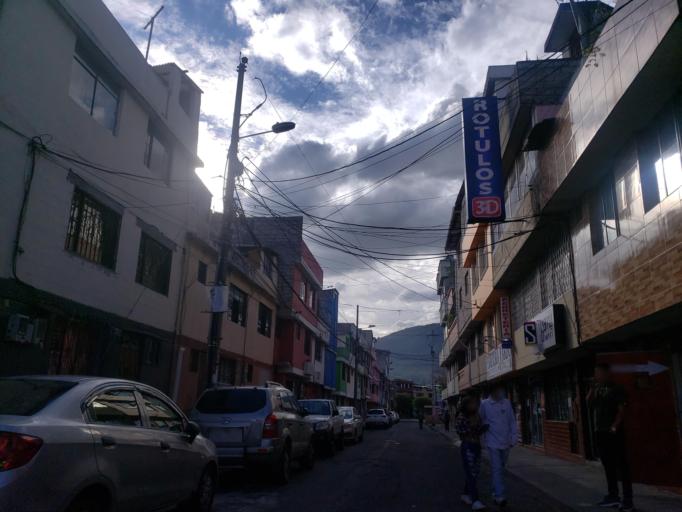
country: EC
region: Pichincha
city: Quito
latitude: -0.2675
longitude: -78.5389
